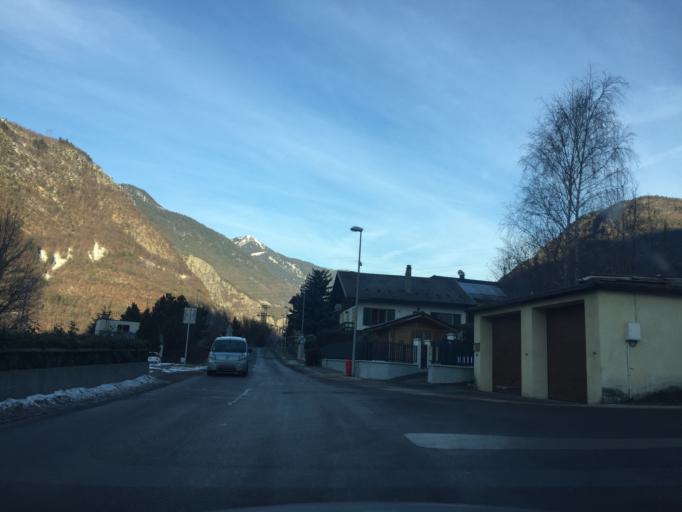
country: FR
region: Rhone-Alpes
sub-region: Departement de la Savoie
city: Aigueblanche
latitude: 45.5149
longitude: 6.4925
